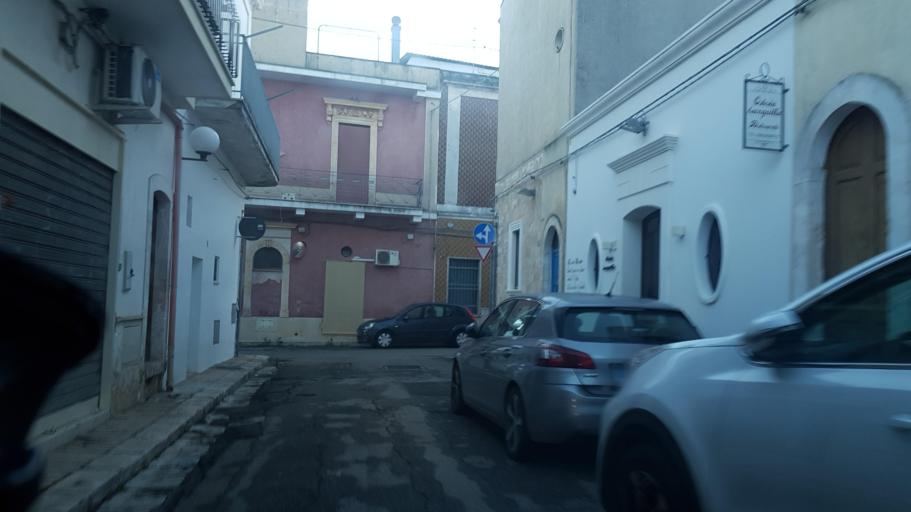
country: IT
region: Apulia
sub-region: Provincia di Brindisi
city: San Michele Salentino
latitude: 40.6306
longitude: 17.6342
